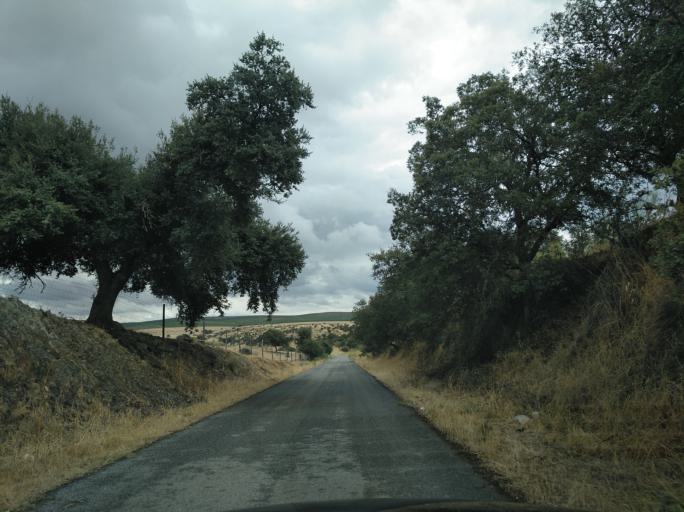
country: PT
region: Portalegre
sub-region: Campo Maior
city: Campo Maior
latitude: 39.0374
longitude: -7.1410
